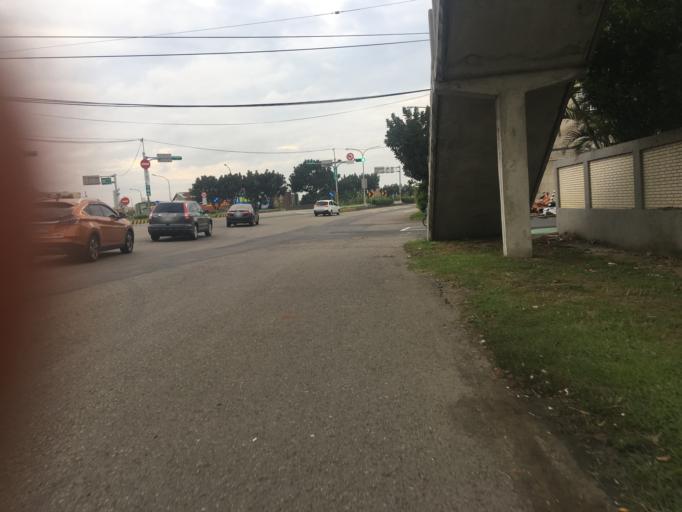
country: TW
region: Taiwan
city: Taoyuan City
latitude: 25.0805
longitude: 121.2150
